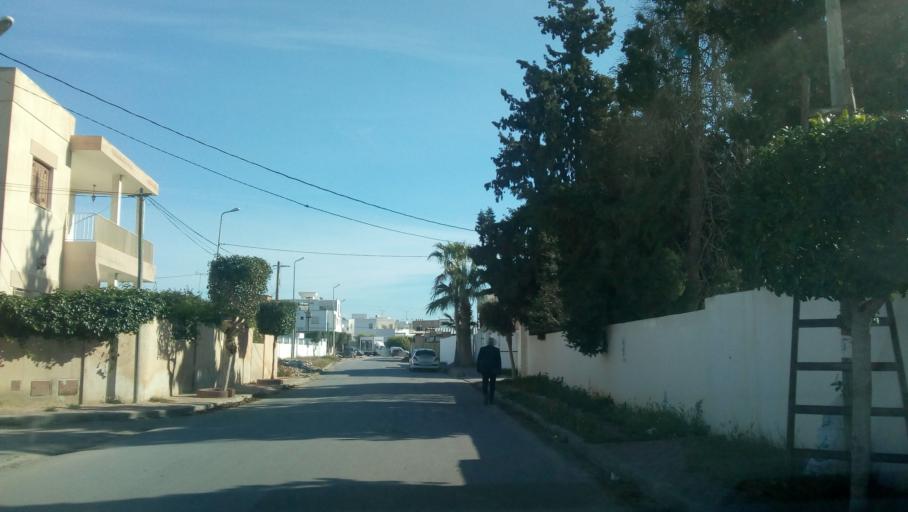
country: TN
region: Safaqis
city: Sfax
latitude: 34.7493
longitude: 10.7401
